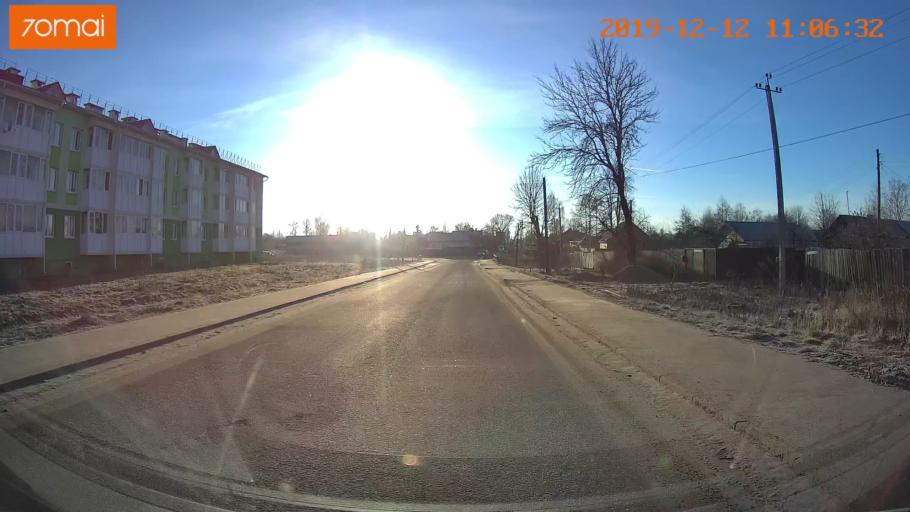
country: RU
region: Ivanovo
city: Kokhma
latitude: 56.9433
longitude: 41.0884
